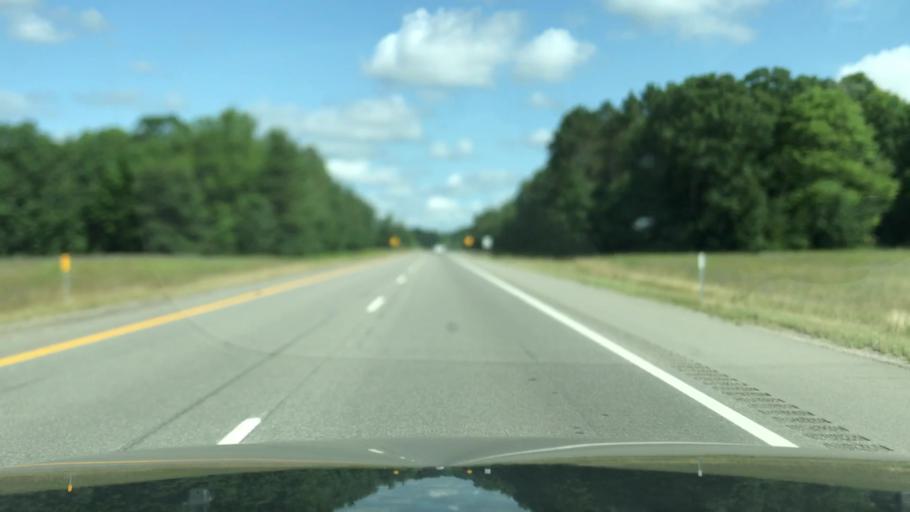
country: US
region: Michigan
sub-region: Mecosta County
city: Big Rapids
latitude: 43.6043
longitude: -85.4907
